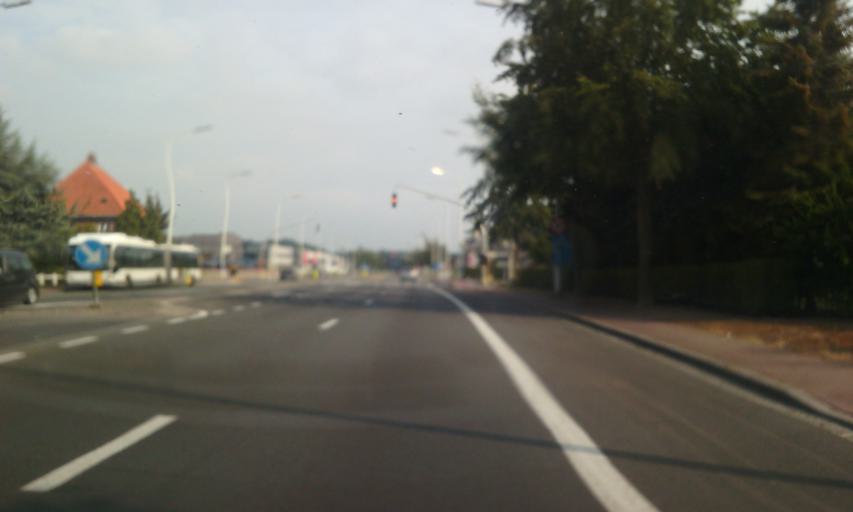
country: BE
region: Flanders
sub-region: Provincie Oost-Vlaanderen
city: Lovendegem
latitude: 51.0990
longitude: 3.6364
